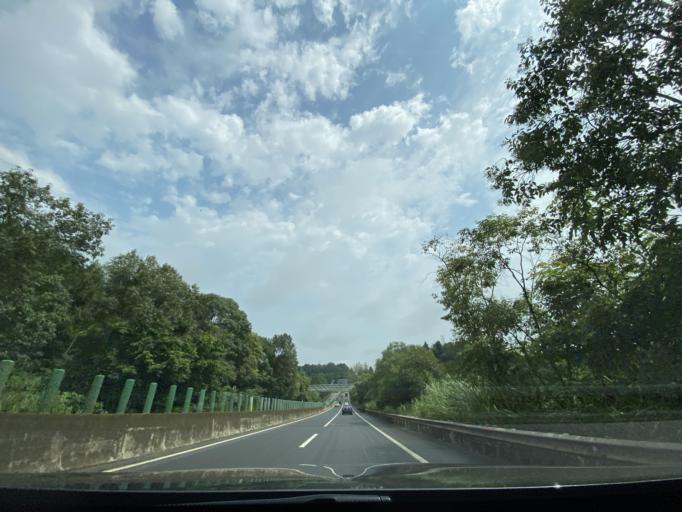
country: CN
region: Sichuan
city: Yanjiang
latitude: 29.9417
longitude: 104.6177
